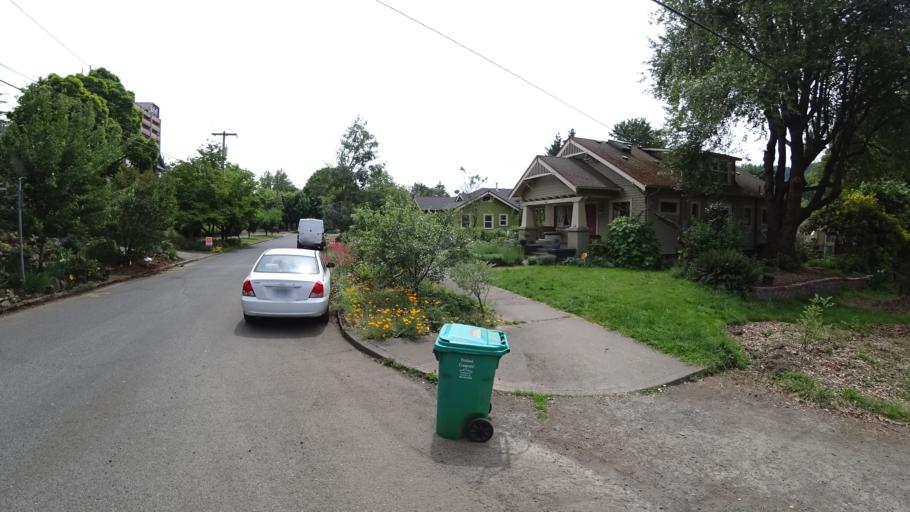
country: US
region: Oregon
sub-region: Washington County
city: West Haven
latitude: 45.5911
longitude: -122.7595
